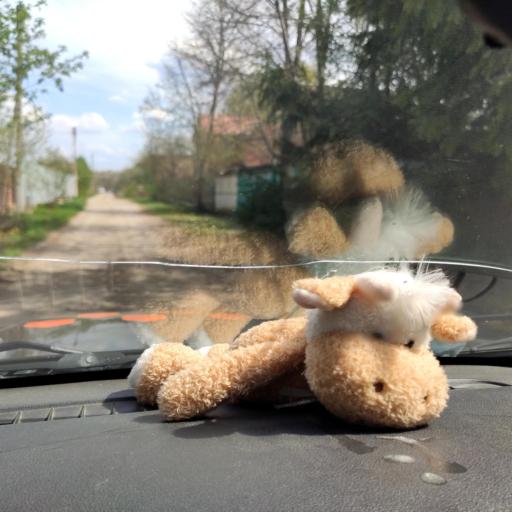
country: RU
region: Samara
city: Podstepki
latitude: 53.5114
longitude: 49.0809
